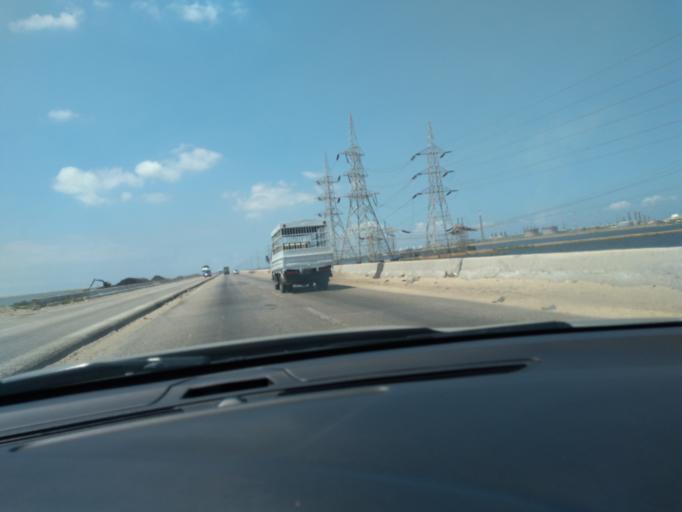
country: EG
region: Muhafazat Bur Sa`id
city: Port Said
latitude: 31.2944
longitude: 32.1619
